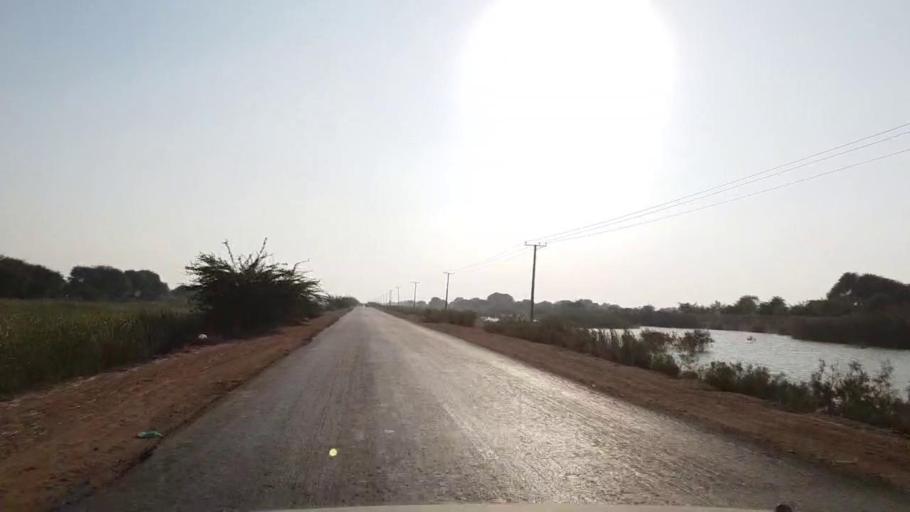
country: PK
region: Sindh
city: Mirpur Batoro
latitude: 24.7744
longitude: 68.2837
